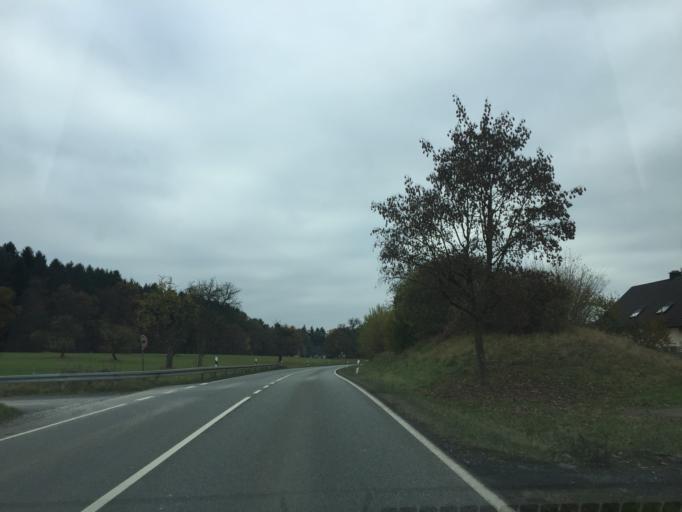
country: DE
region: Rheinland-Pfalz
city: Grossholbach
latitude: 50.4432
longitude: 7.8973
